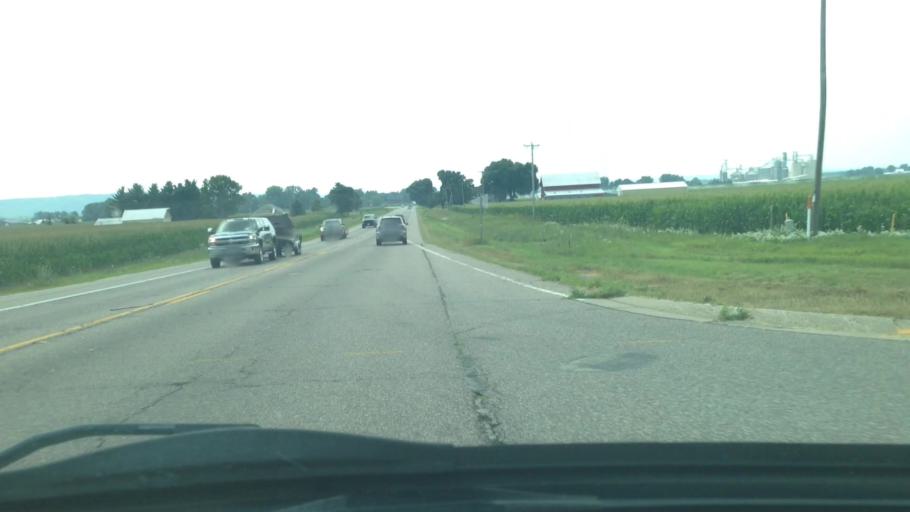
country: US
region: Wisconsin
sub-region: Sauk County
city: Prairie du Sac
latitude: 43.2818
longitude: -89.7592
